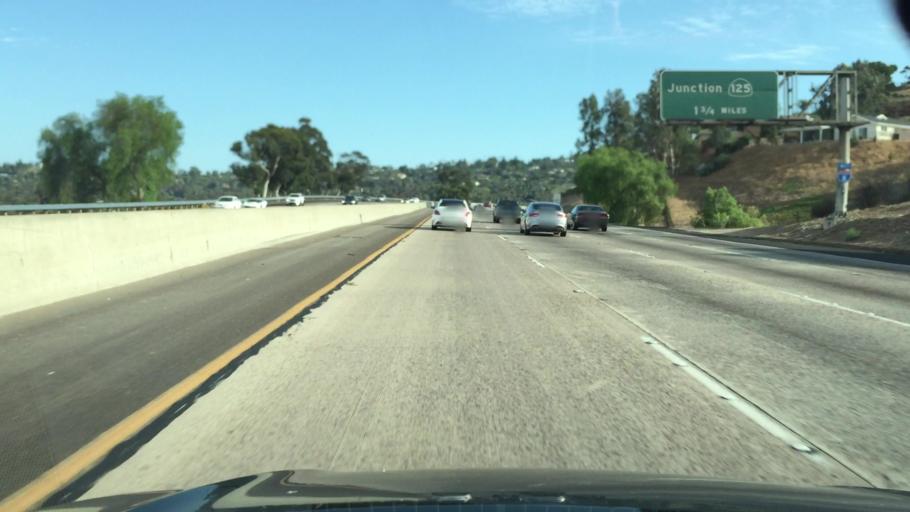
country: US
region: California
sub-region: San Diego County
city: El Cajon
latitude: 32.7903
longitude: -116.9779
